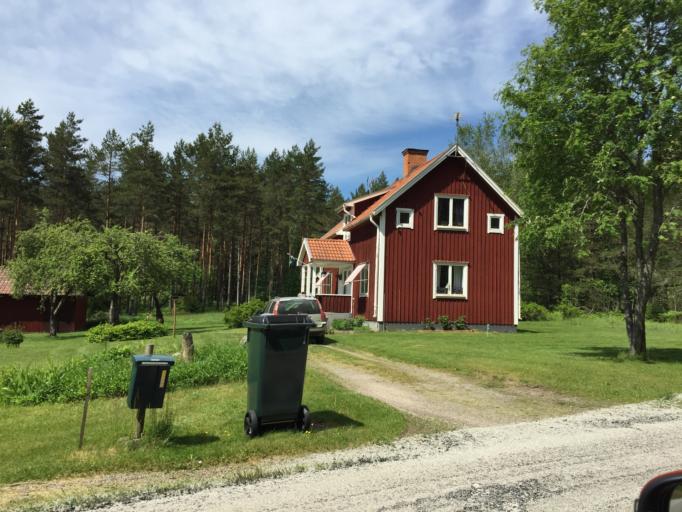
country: SE
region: Soedermanland
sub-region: Vingakers Kommun
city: Vingaker
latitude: 58.9796
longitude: 15.6808
